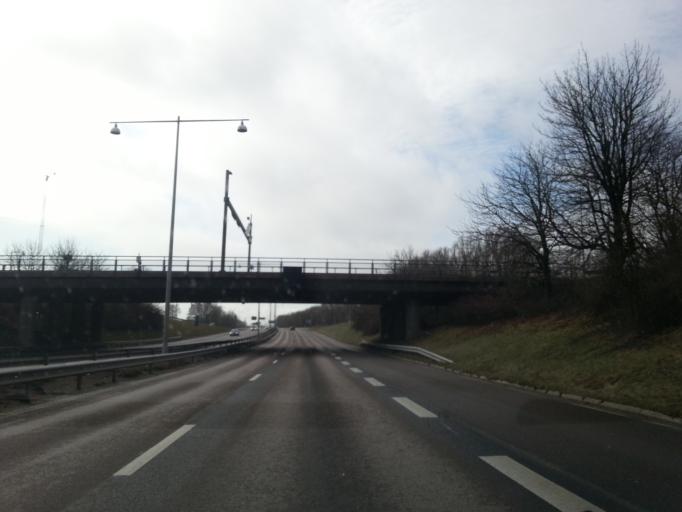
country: SE
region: Vaestra Goetaland
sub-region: Goteborg
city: Hammarkullen
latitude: 57.7589
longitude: 11.9919
